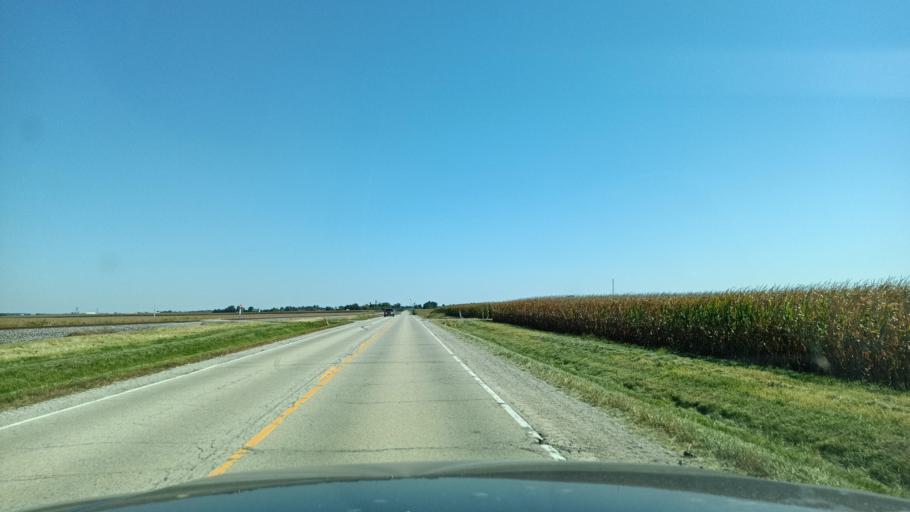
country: US
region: Illinois
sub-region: Tazewell County
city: Mackinaw
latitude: 40.6268
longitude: -89.3173
